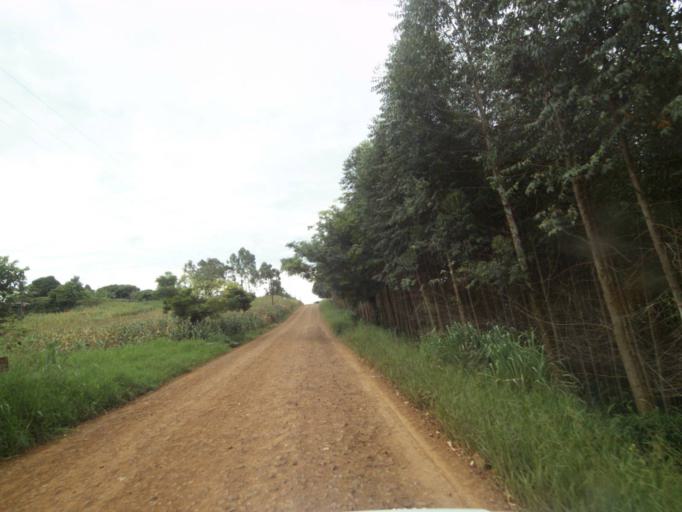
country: BR
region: Parana
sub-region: Guaraniacu
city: Guaraniacu
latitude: -24.9117
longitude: -52.9360
